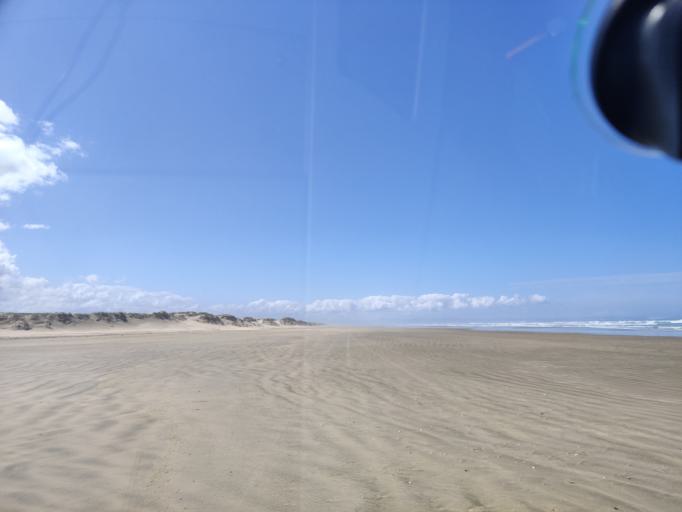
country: NZ
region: Northland
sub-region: Far North District
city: Ahipara
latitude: -34.9016
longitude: 173.0862
